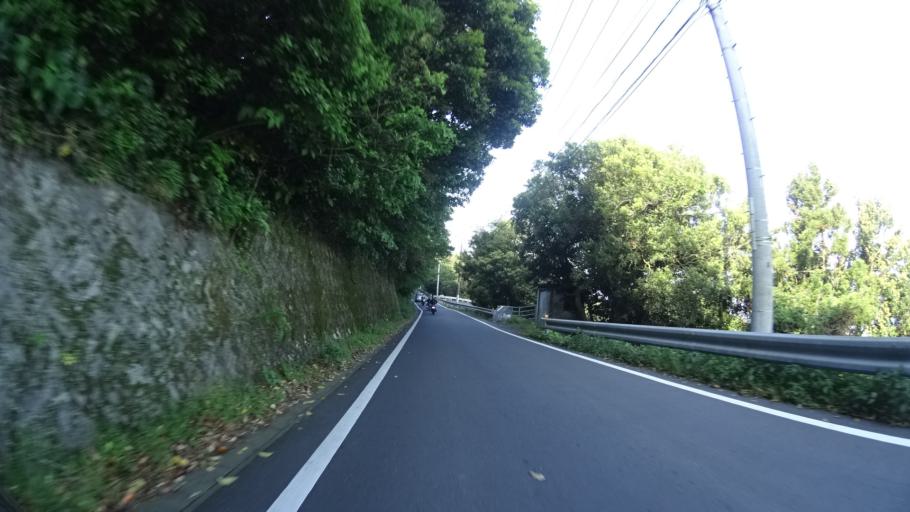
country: JP
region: Ehime
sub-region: Nishiuwa-gun
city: Ikata-cho
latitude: 33.3797
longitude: 132.0666
